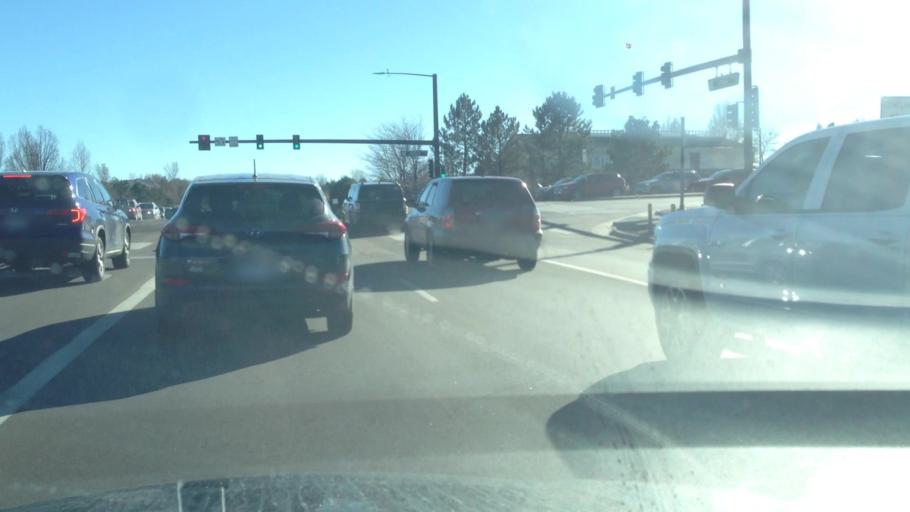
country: US
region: Colorado
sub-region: Douglas County
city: Stonegate
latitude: 39.5342
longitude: -104.7934
